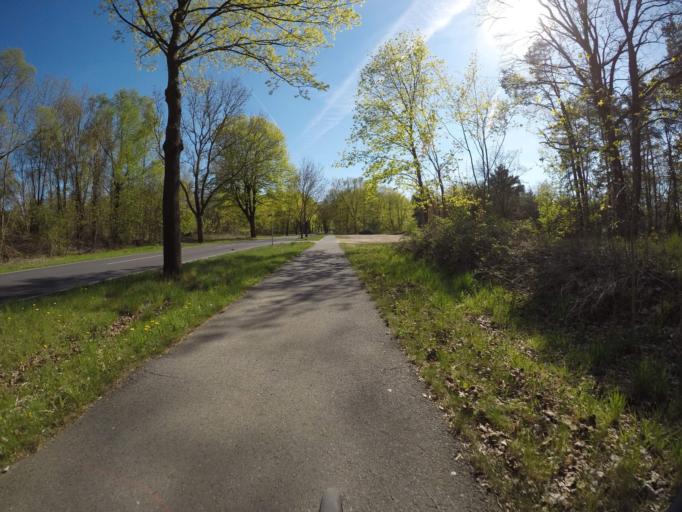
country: DE
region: Brandenburg
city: Rehfelde
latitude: 52.4860
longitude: 13.9140
